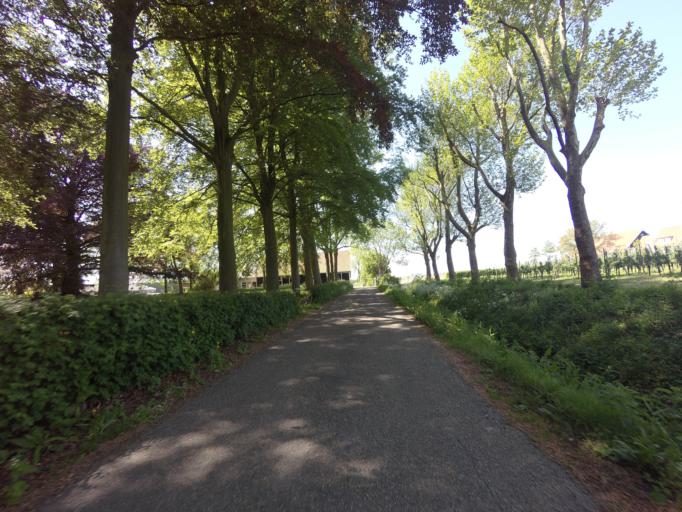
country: NL
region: Zeeland
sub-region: Gemeente Goes
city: Goes
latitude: 51.4685
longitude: 3.9518
